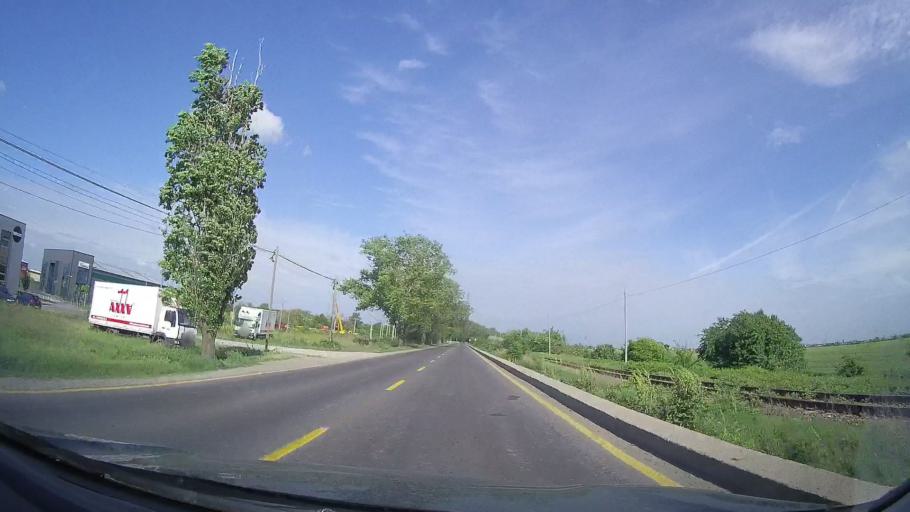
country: RO
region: Ilfov
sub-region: Comuna Magurele
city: Magurele
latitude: 44.3616
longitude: 26.0292
